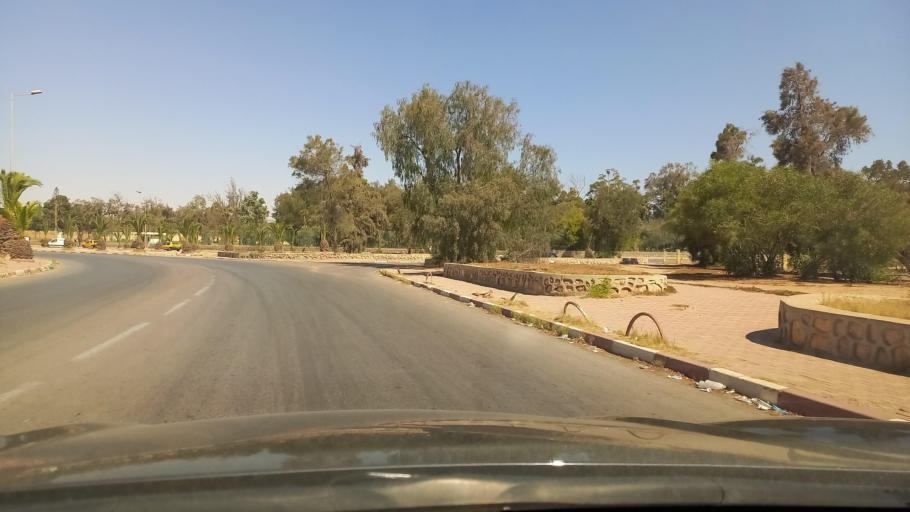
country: TN
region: Safaqis
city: Sfax
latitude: 34.7328
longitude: 10.7443
